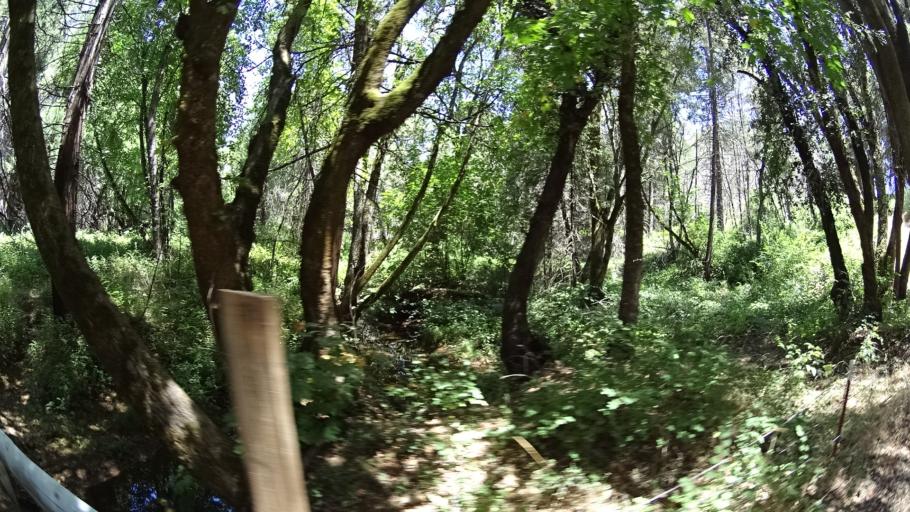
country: US
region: California
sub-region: Calaveras County
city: Mountain Ranch
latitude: 38.2743
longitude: -120.5916
